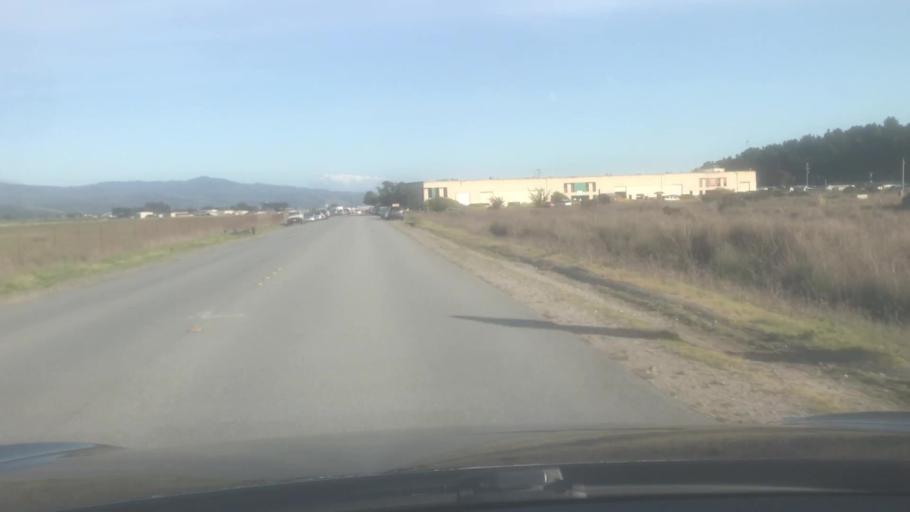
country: US
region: California
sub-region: San Mateo County
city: Moss Beach
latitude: 37.5129
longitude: -122.5022
